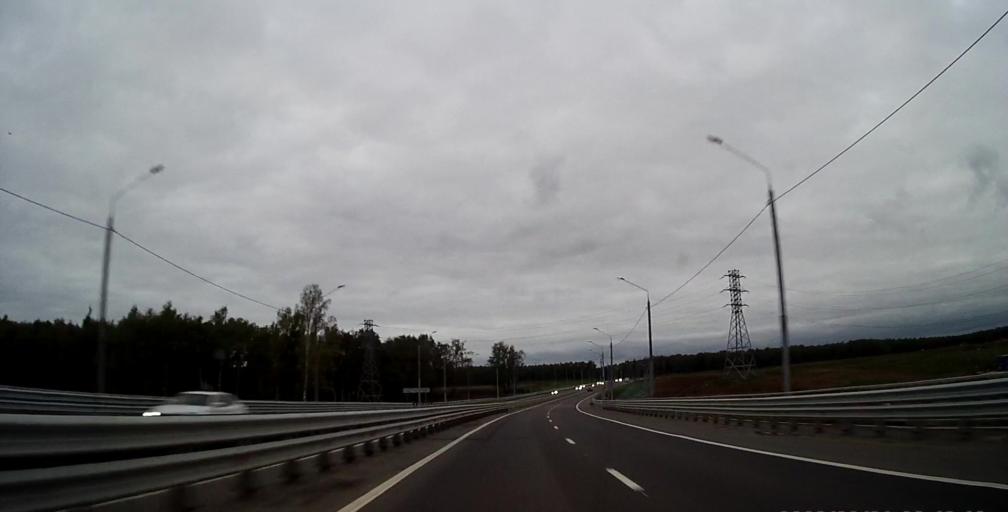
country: RU
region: Moskovskaya
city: Klimovsk
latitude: 55.3951
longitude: 37.5027
